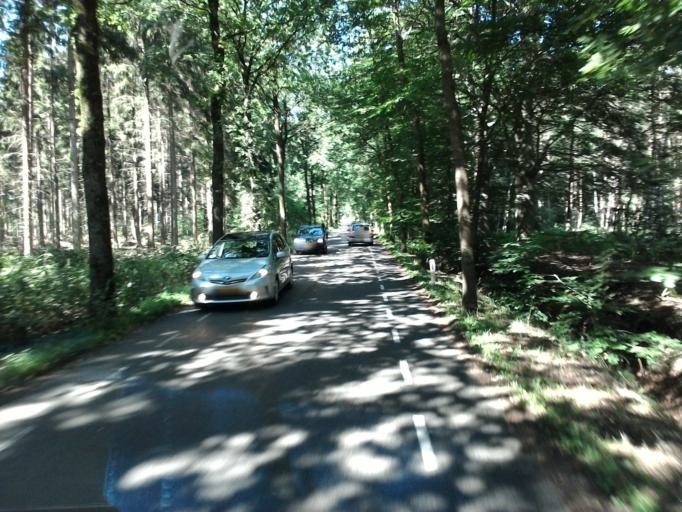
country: NL
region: Utrecht
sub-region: Gemeente Soest
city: Soest
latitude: 52.1721
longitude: 5.2227
